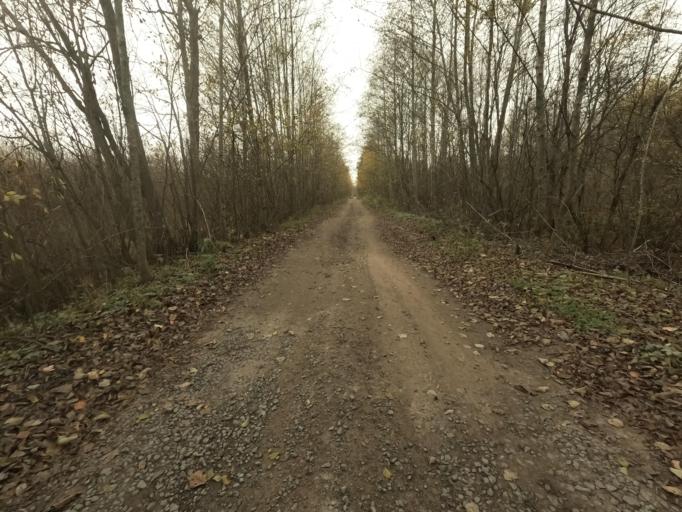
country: RU
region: Leningrad
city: Pavlovo
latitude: 59.7880
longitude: 30.8860
